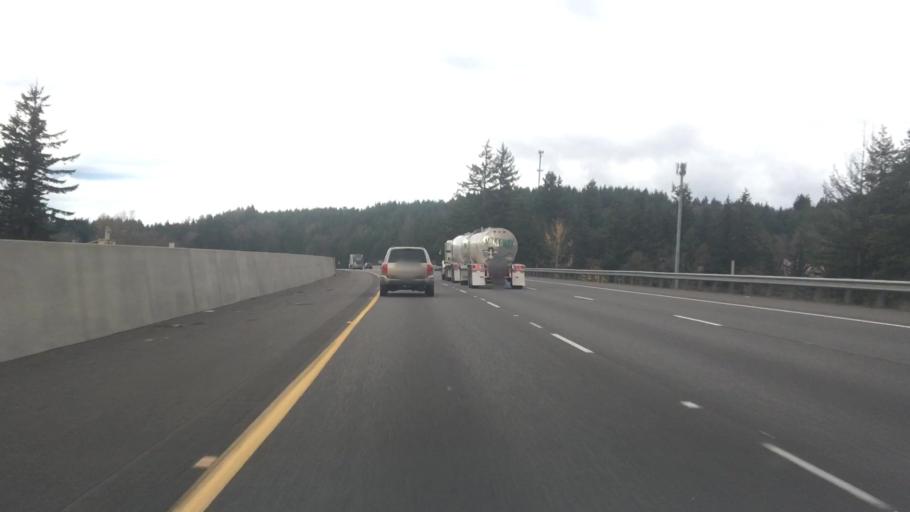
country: US
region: Washington
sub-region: Lewis County
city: Fords Prairie
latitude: 46.7334
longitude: -122.9753
